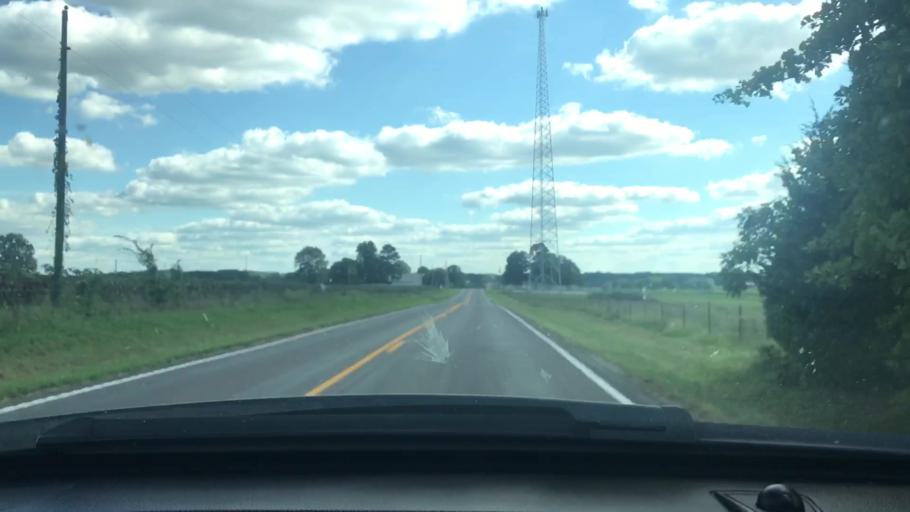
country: US
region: Missouri
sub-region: Wright County
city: Mountain Grove
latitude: 37.2498
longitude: -92.3003
